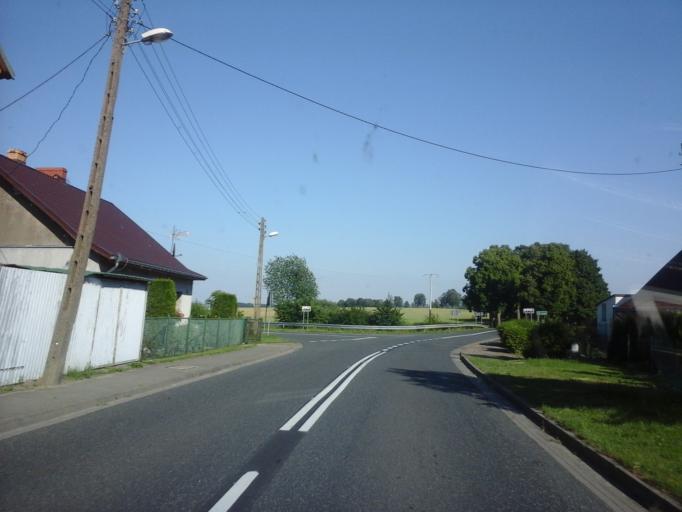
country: PL
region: West Pomeranian Voivodeship
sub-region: Powiat lobeski
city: Dobra
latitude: 53.6476
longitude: 15.2246
